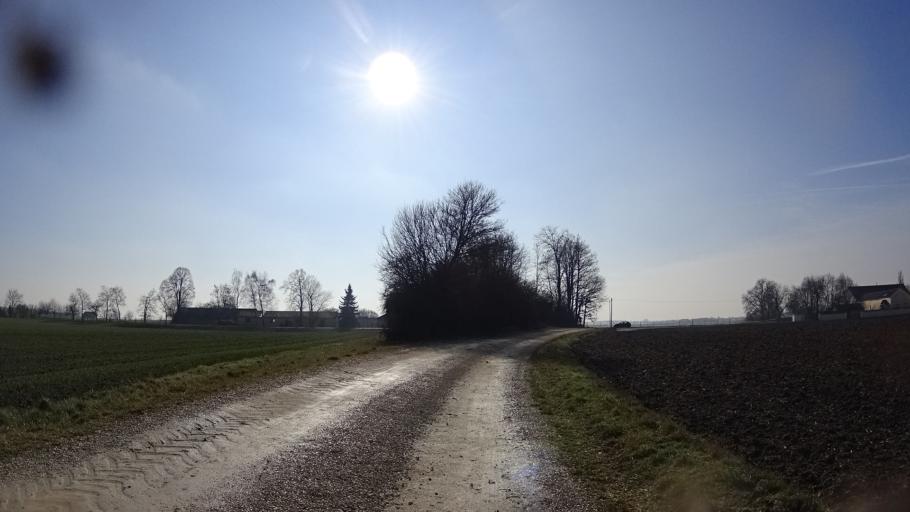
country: DE
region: Bavaria
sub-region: Upper Bavaria
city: Wettstetten
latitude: 48.8284
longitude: 11.3892
